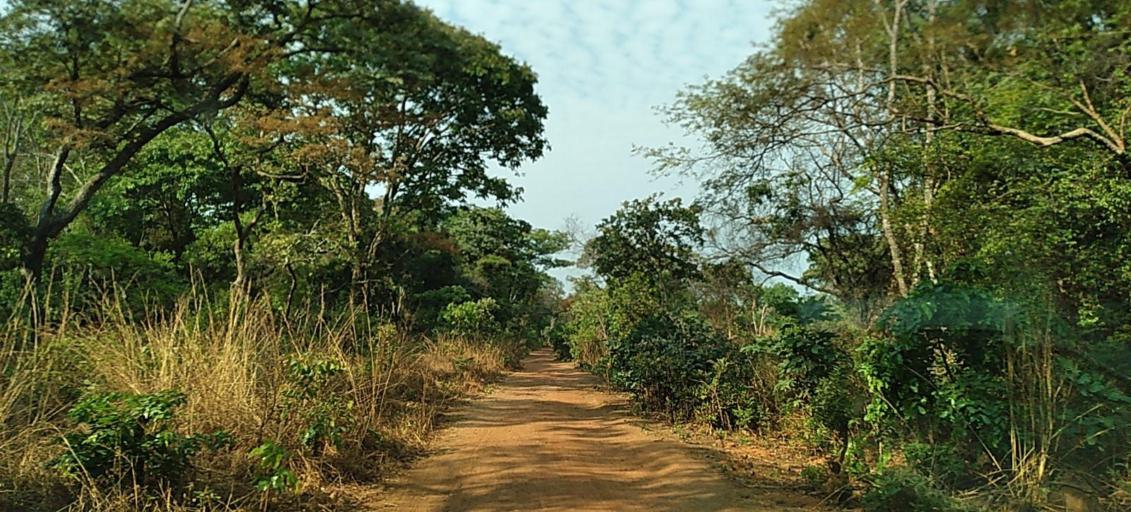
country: ZM
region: Copperbelt
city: Kalulushi
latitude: -12.9883
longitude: 27.7189
